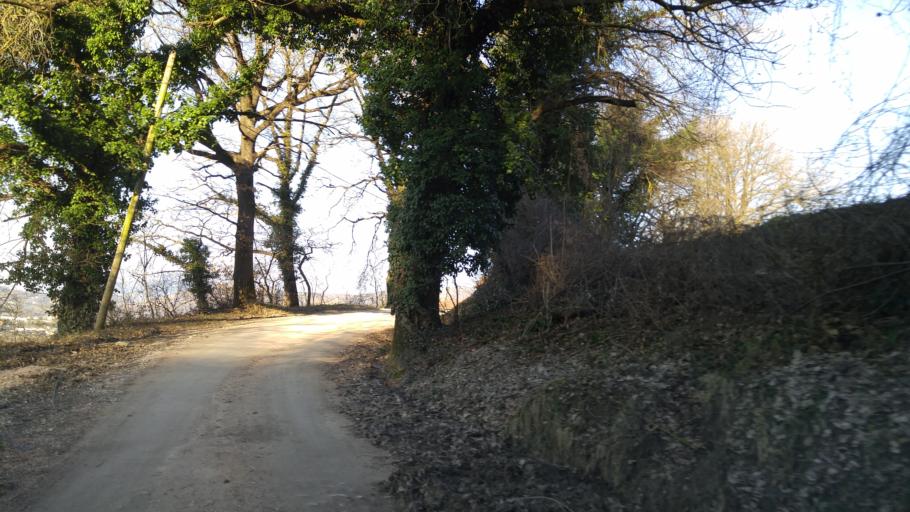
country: IT
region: The Marches
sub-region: Provincia di Pesaro e Urbino
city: Cagli
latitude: 43.5563
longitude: 12.6609
